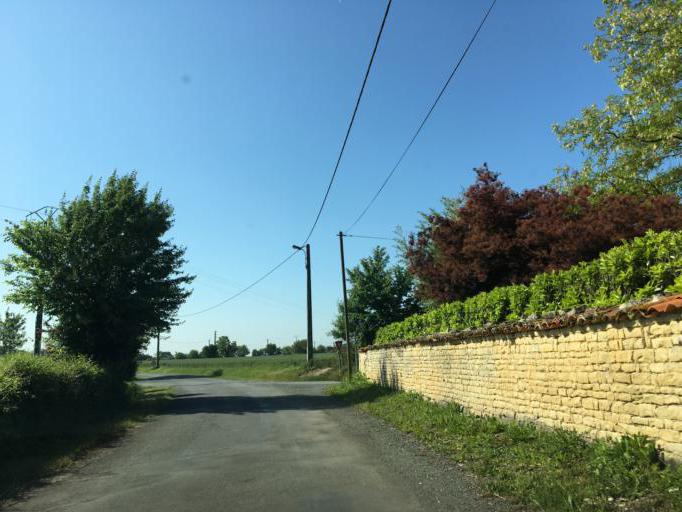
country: FR
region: Poitou-Charentes
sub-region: Departement des Deux-Sevres
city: Beauvoir-sur-Niort
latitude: 46.0931
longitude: -0.5067
